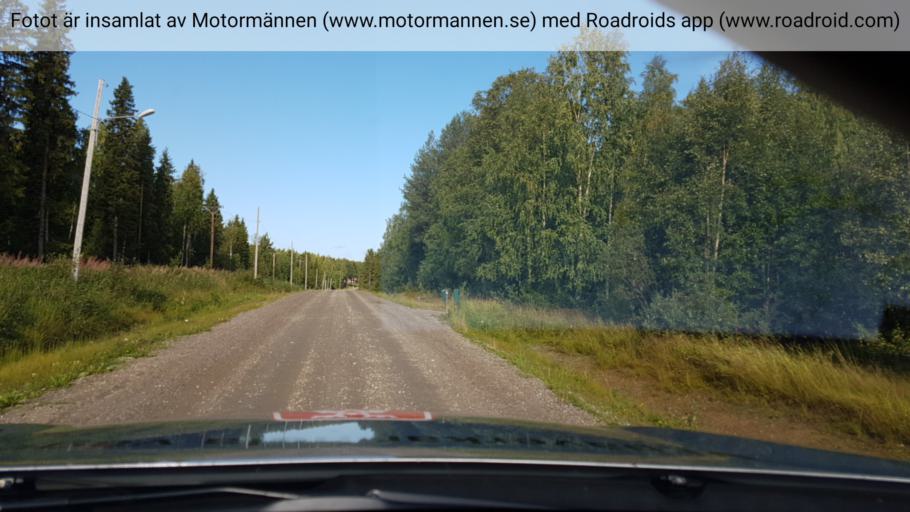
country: SE
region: Norrbotten
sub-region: Kalix Kommun
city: Kalix
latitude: 66.1169
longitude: 23.2764
